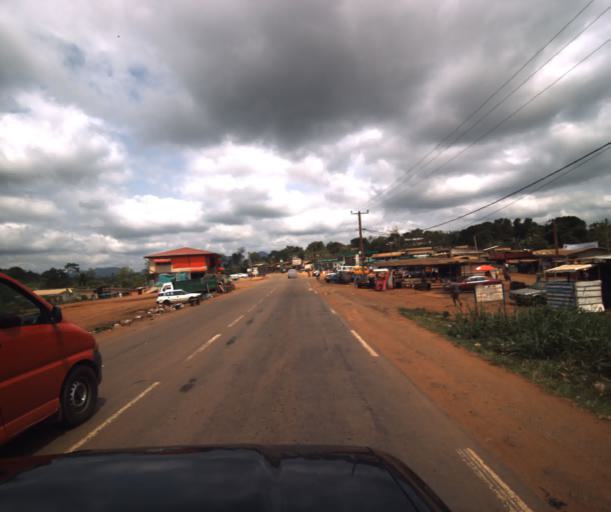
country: CM
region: Centre
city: Mbankomo
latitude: 3.7896
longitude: 11.3999
